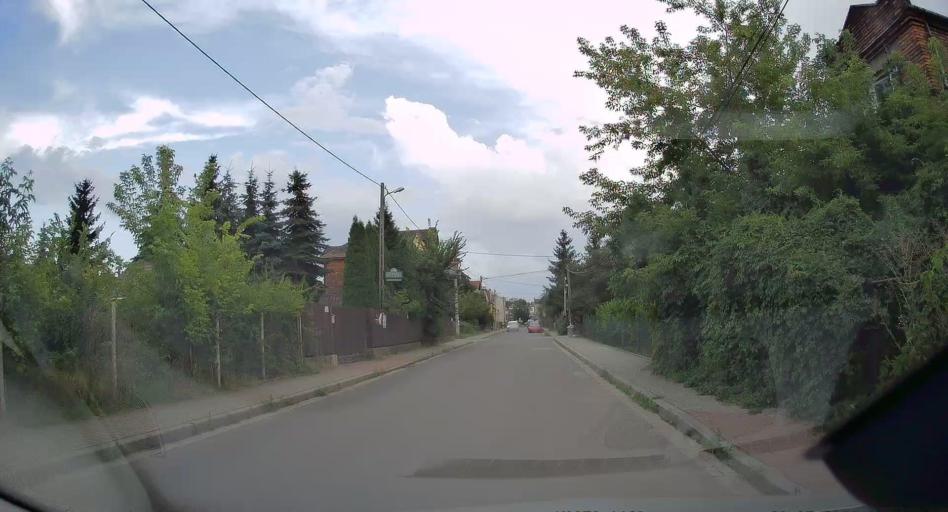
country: PL
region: Lesser Poland Voivodeship
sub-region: Krakow
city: Krakow
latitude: 50.0258
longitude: 19.9962
